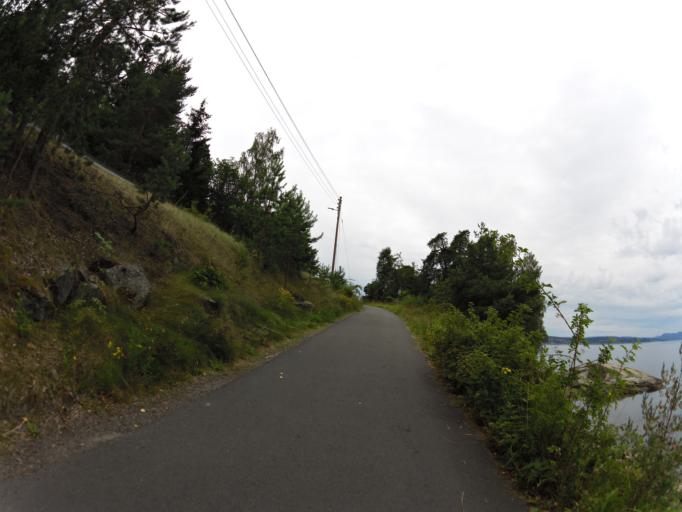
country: NO
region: Akershus
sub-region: Oppegard
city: Kolbotn
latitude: 59.8313
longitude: 10.7692
